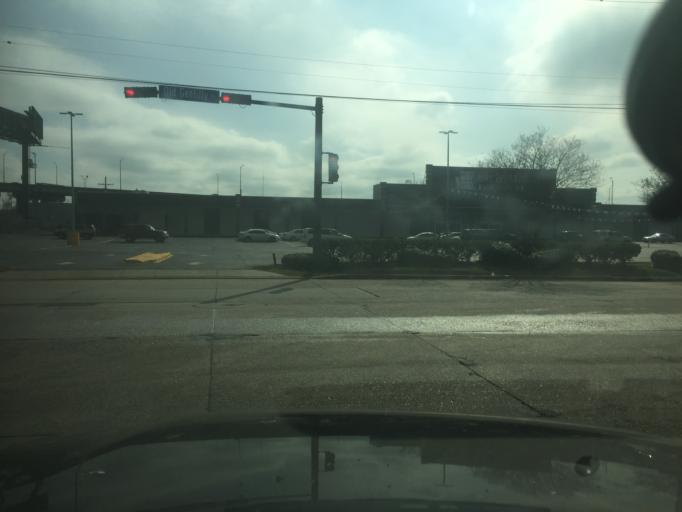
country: US
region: Louisiana
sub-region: Saint Bernard Parish
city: Arabi
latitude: 30.0052
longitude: -90.0336
